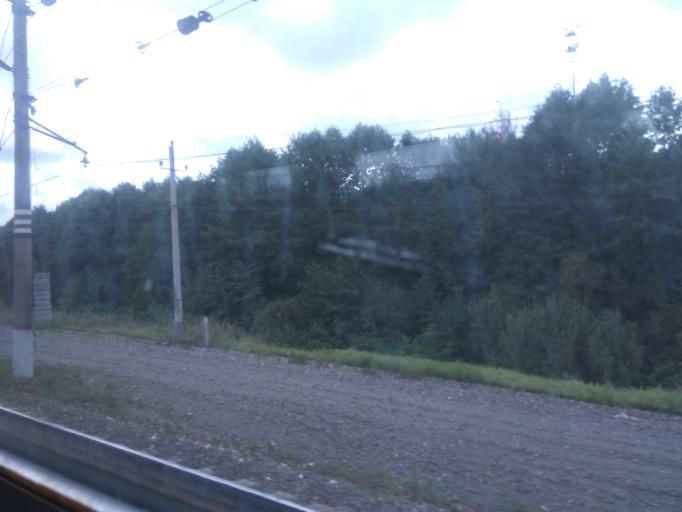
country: RU
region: Moskovskaya
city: Beloozerskiy
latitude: 55.4485
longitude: 38.4861
